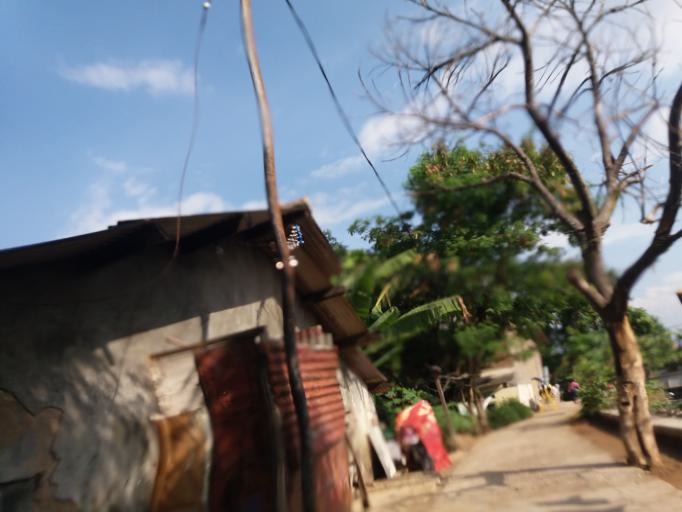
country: ID
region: West Java
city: Bandung
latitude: -6.9318
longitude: 107.6670
